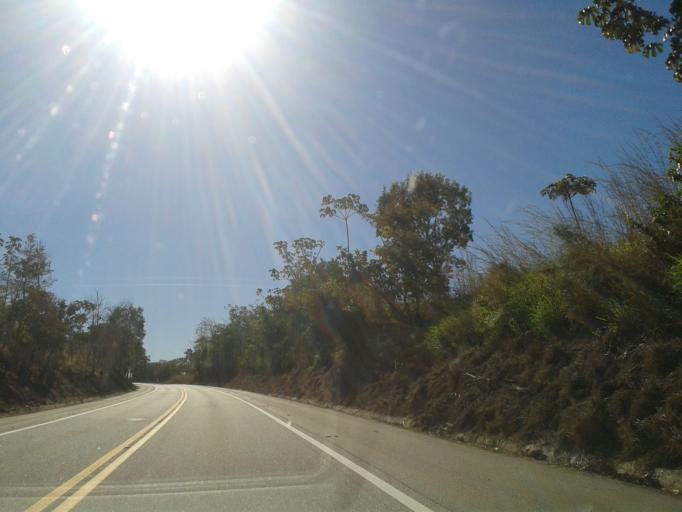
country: BR
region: Goias
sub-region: Itapuranga
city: Itapuranga
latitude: -15.6182
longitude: -50.2408
